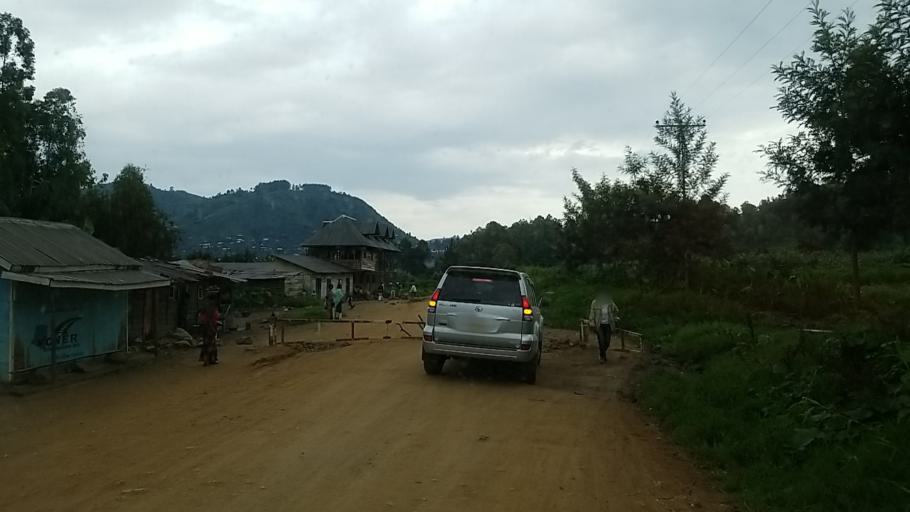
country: CD
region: Nord Kivu
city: Sake
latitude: -1.7000
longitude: 29.0139
